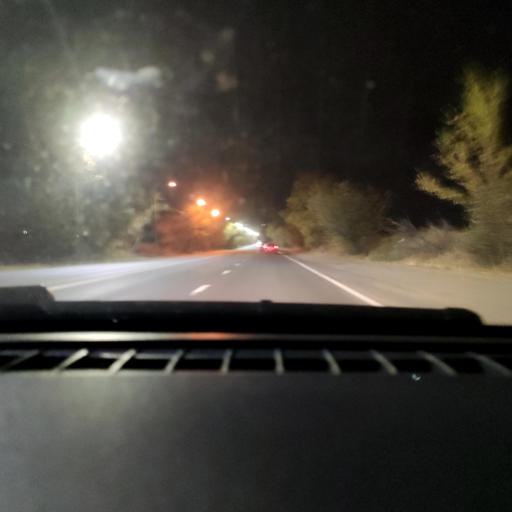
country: RU
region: Voronezj
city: Maslovka
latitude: 51.6241
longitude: 39.2801
